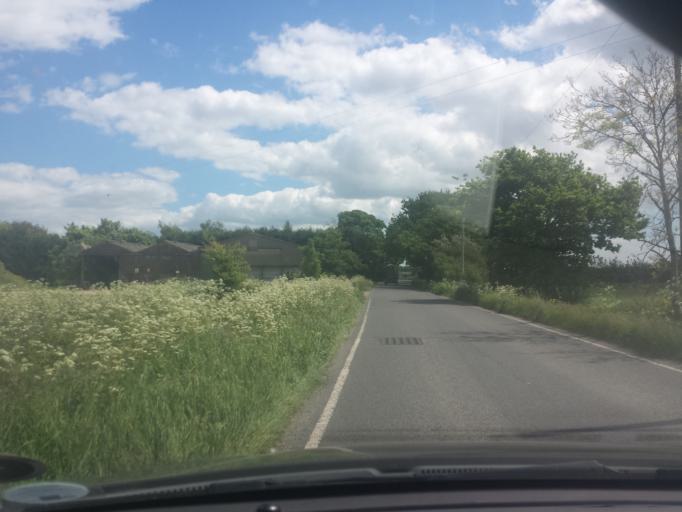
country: GB
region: England
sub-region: Essex
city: Little Clacton
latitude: 51.8901
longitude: 1.1513
